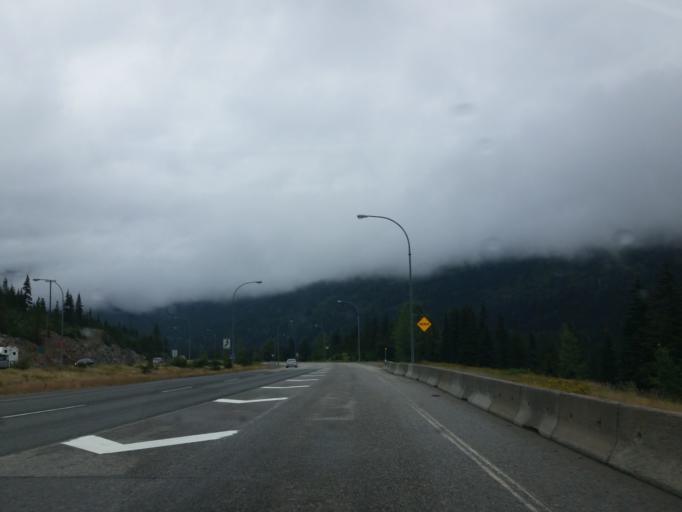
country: CA
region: British Columbia
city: Hope
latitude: 49.6322
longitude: -121.0122
